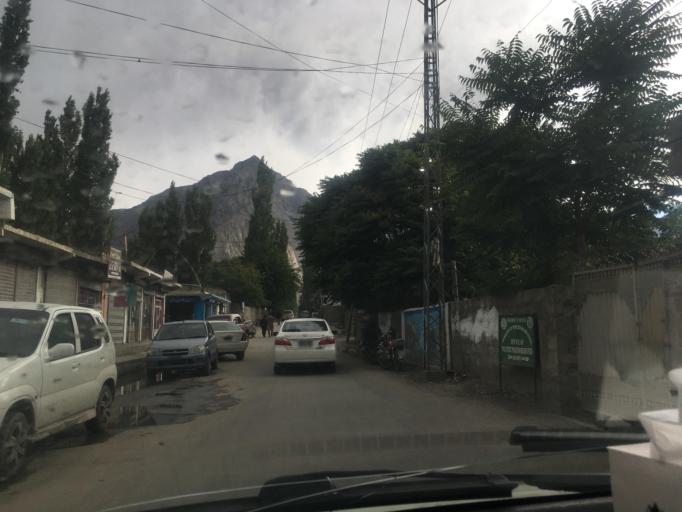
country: PK
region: Gilgit-Baltistan
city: Skardu
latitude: 35.2938
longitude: 75.6496
